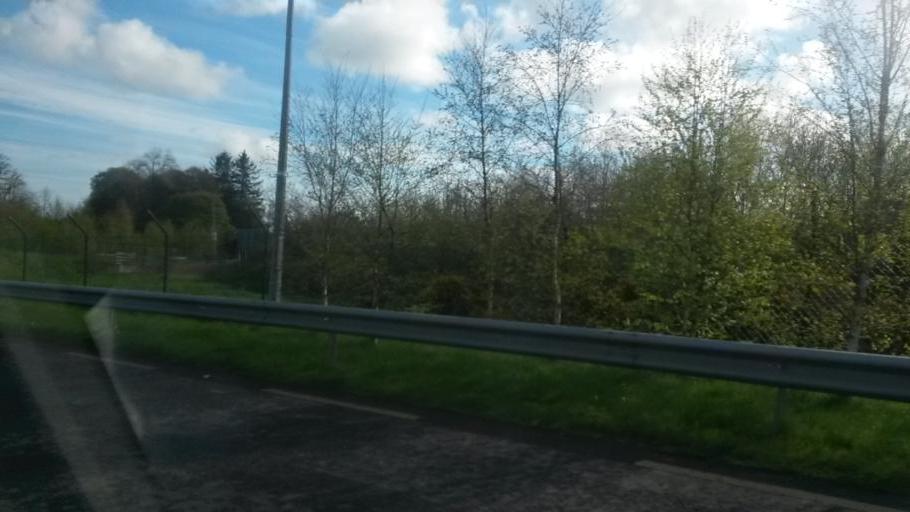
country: IE
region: Leinster
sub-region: An Mhi
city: Kells
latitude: 53.7190
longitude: -6.8474
